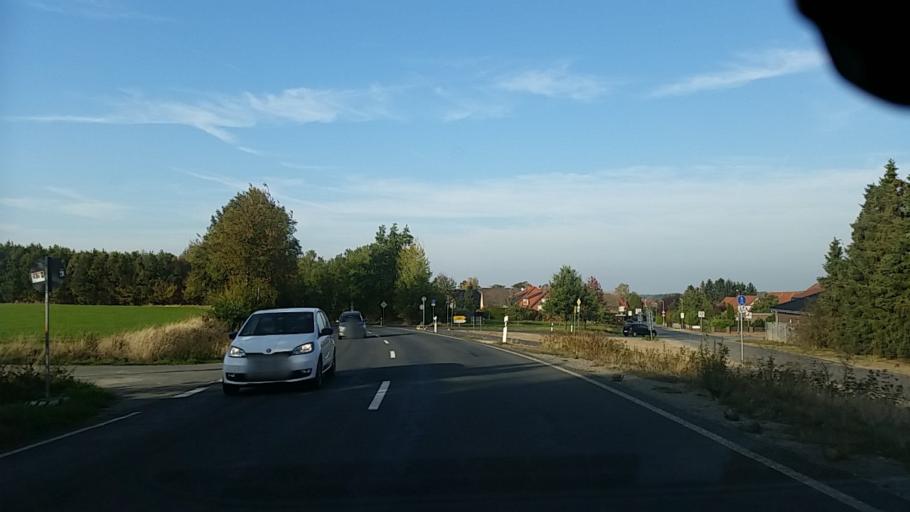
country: DE
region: Lower Saxony
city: Gross Twulpstedt
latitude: 52.3848
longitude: 10.8517
